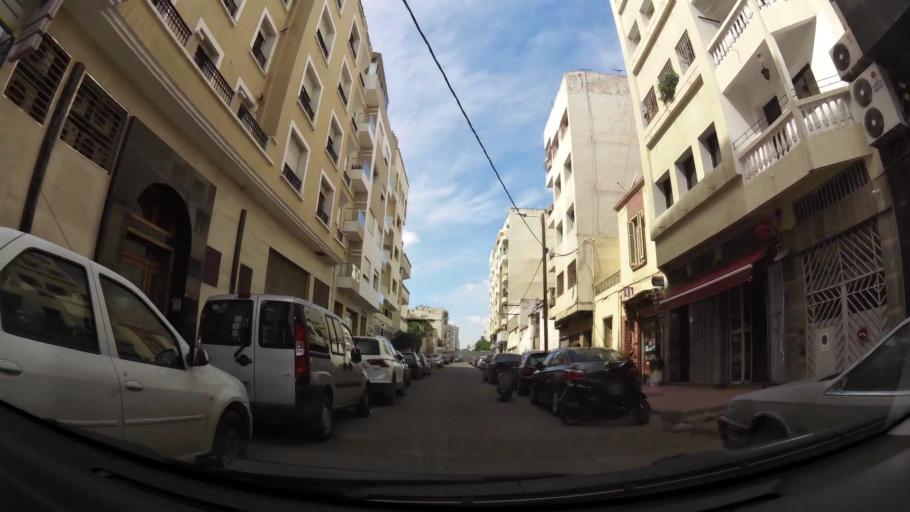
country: MA
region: Grand Casablanca
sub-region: Casablanca
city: Casablanca
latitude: 33.5812
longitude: -7.6422
